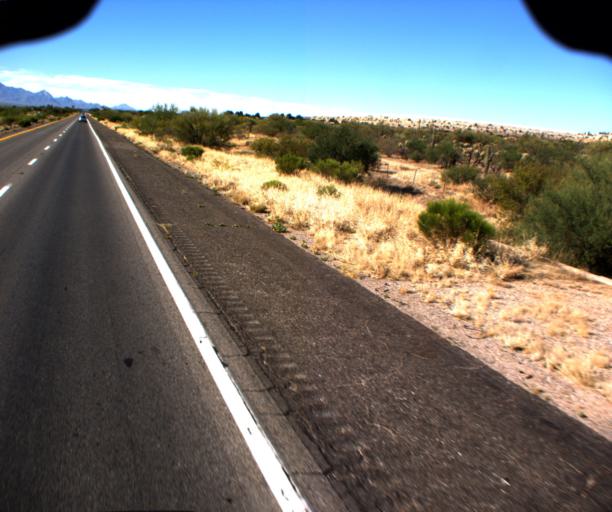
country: US
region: Arizona
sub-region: Pima County
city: Sahuarita
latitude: 31.9713
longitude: -110.9897
